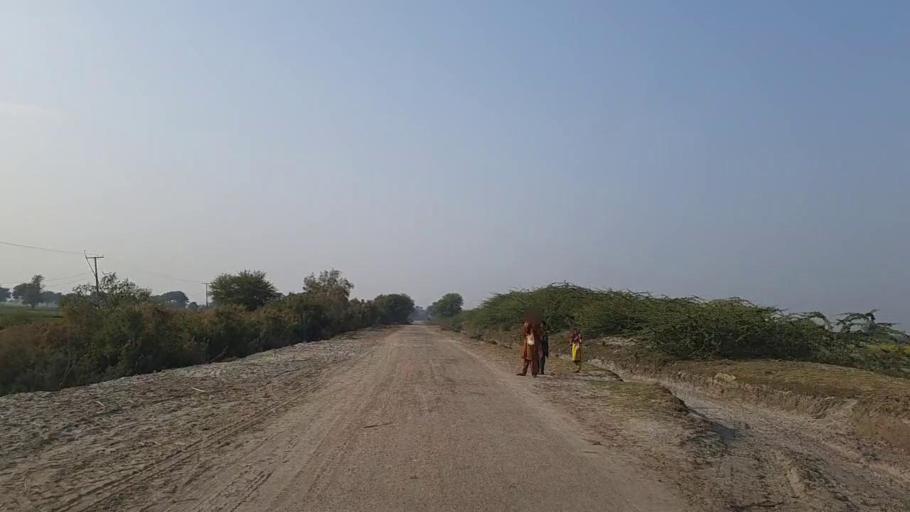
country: PK
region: Sindh
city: Nawabshah
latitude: 26.3430
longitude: 68.4891
